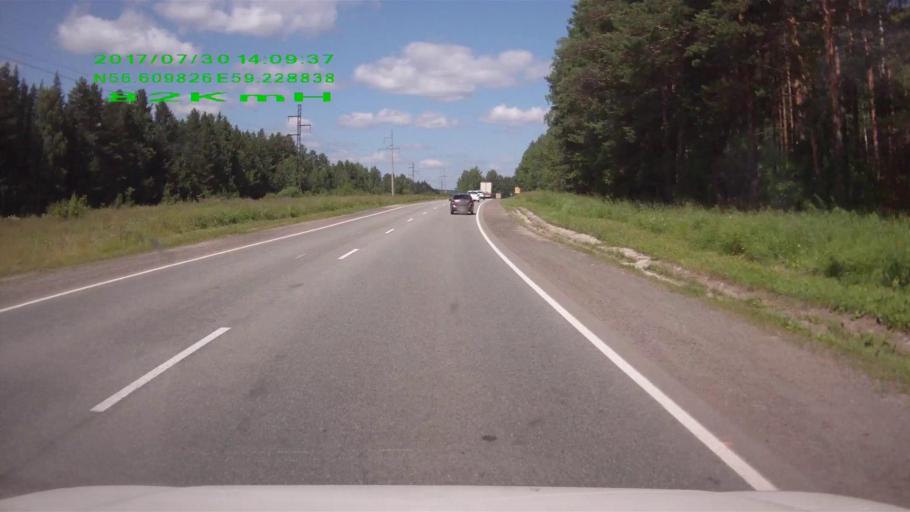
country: RU
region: Sverdlovsk
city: Nizhniye Sergi
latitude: 56.6102
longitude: 59.2289
